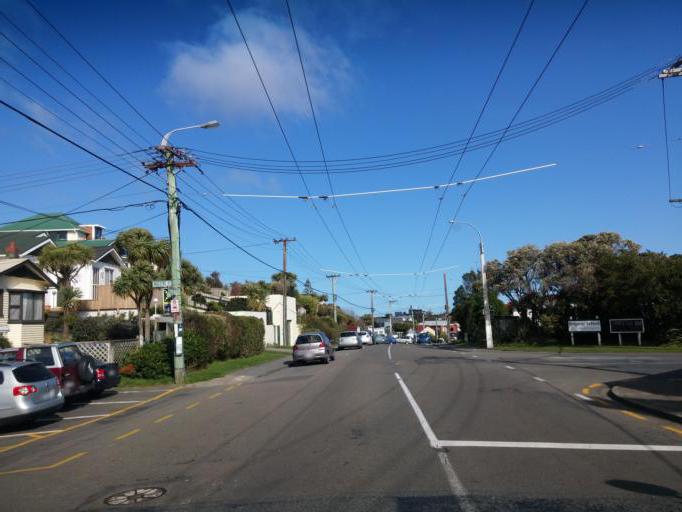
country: NZ
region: Wellington
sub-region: Wellington City
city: Brooklyn
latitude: -41.3154
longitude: 174.7653
